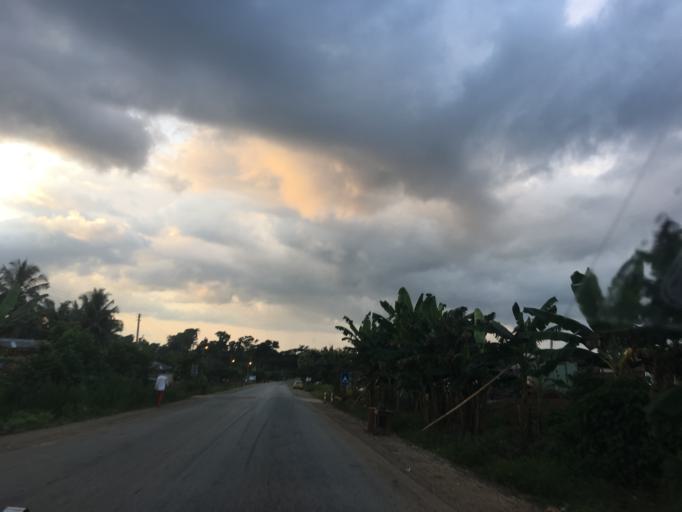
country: GH
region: Western
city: Bibiani
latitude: 6.7488
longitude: -2.5044
